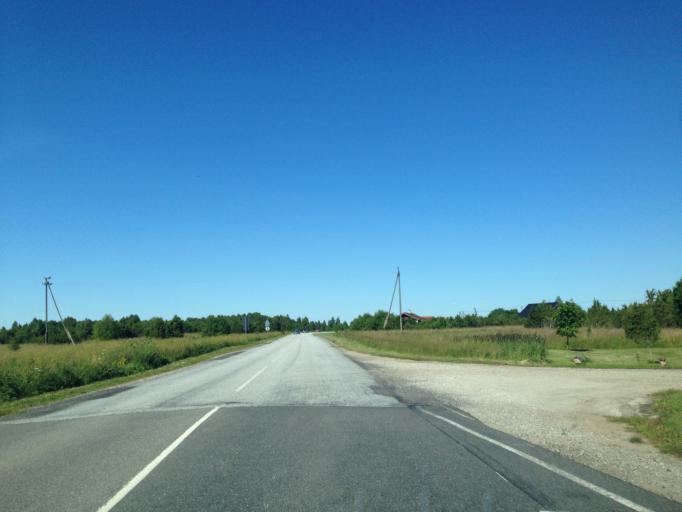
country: EE
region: Harju
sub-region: Raasiku vald
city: Raasiku
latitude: 59.4524
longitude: 25.2009
